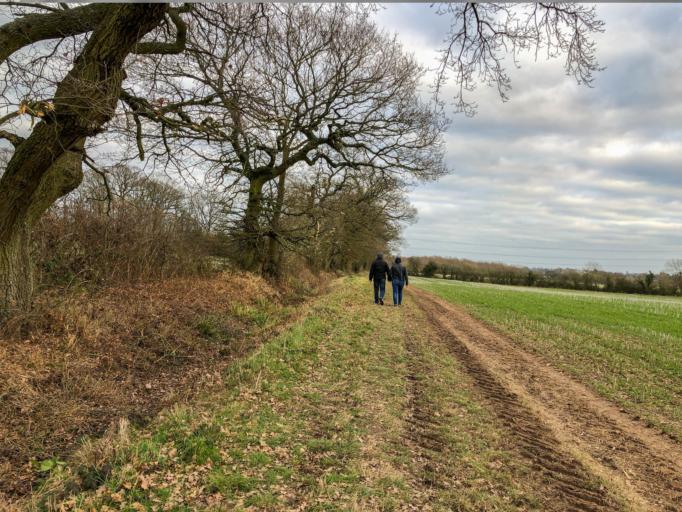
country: GB
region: England
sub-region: Warwickshire
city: Kenilworth
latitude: 52.3491
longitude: -1.6190
